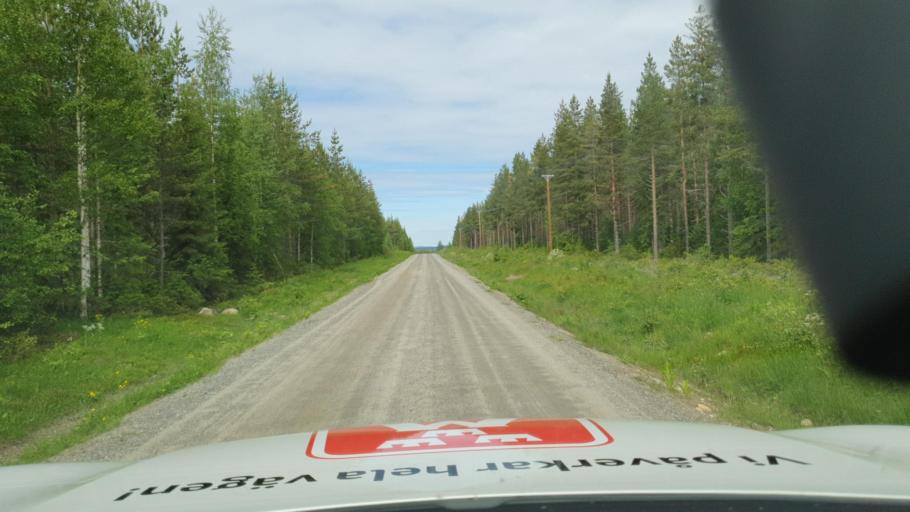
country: SE
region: Vaesterbotten
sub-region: Skelleftea Kommun
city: Langsele
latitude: 64.6035
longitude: 20.2805
